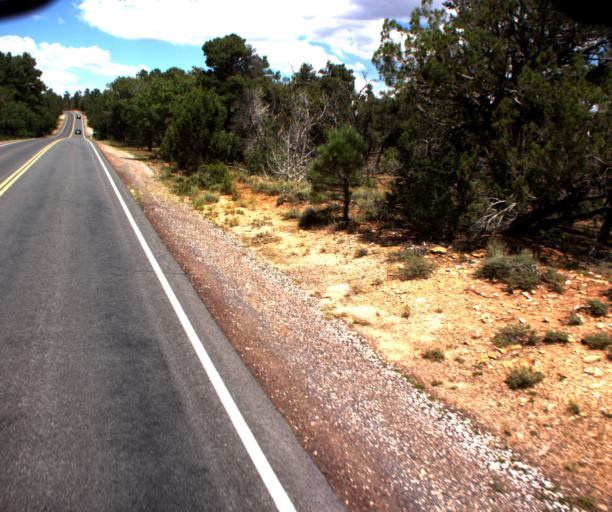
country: US
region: Arizona
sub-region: Coconino County
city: Grand Canyon
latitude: 36.0217
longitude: -112.0655
